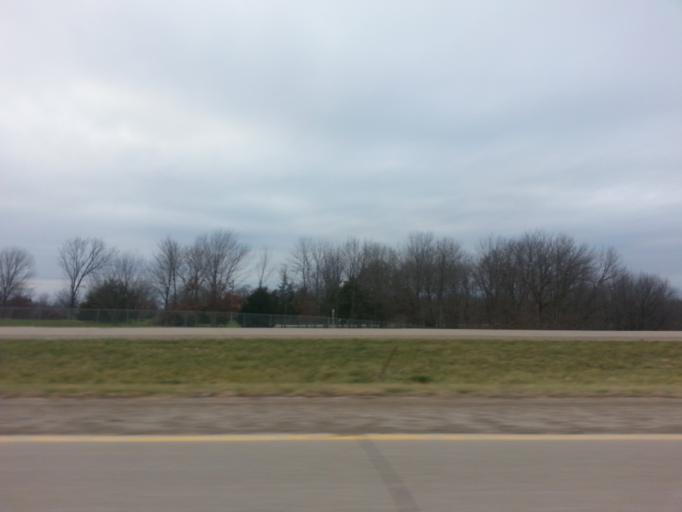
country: US
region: Iowa
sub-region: Henry County
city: Mount Pleasant
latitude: 40.9308
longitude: -91.5386
